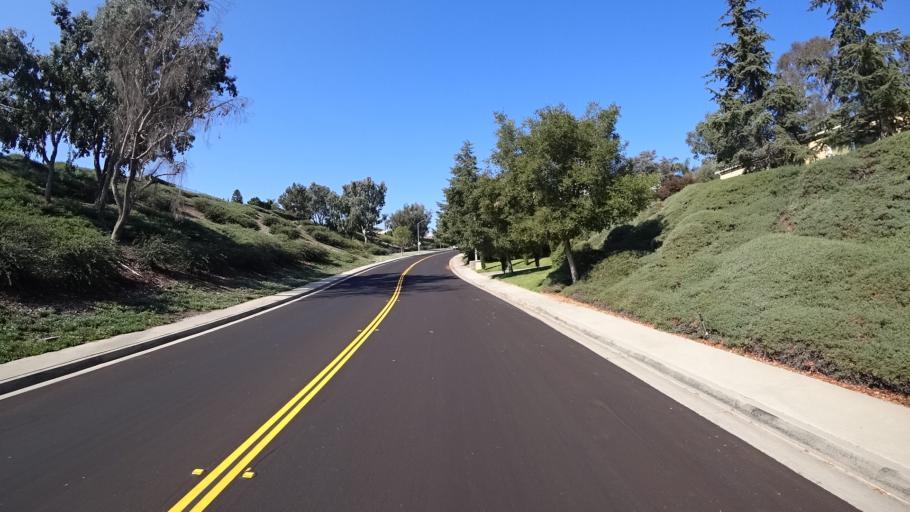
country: US
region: California
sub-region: Orange County
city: San Juan Capistrano
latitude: 33.4778
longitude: -117.6292
